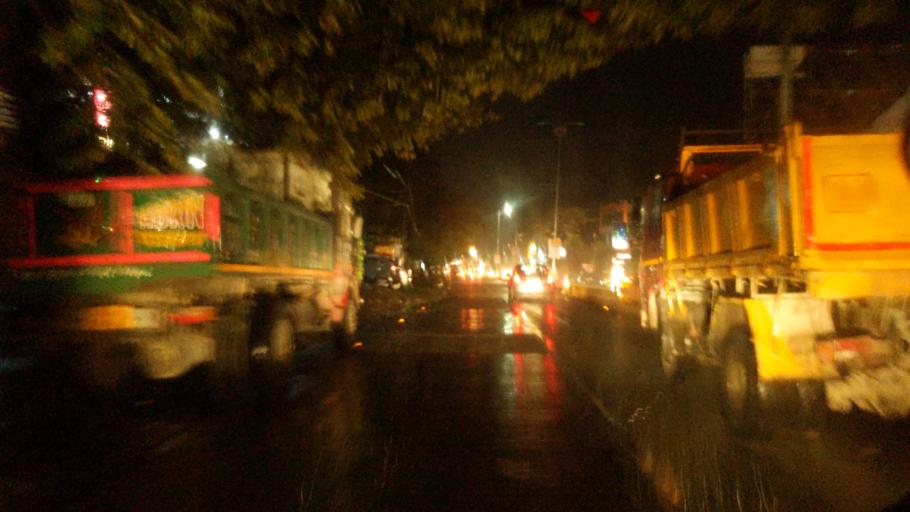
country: IN
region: Uttarakhand
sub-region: Naini Tal
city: Haldwani
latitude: 29.2481
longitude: 79.5387
